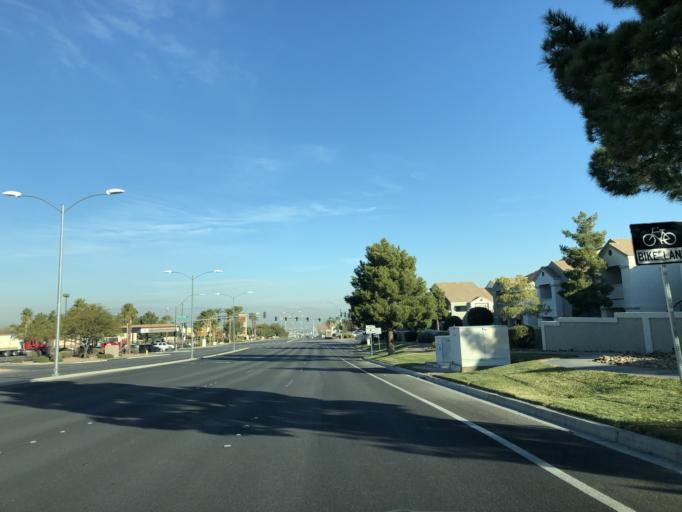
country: US
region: Nevada
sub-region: Clark County
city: Whitney
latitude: 36.0202
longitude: -115.0472
